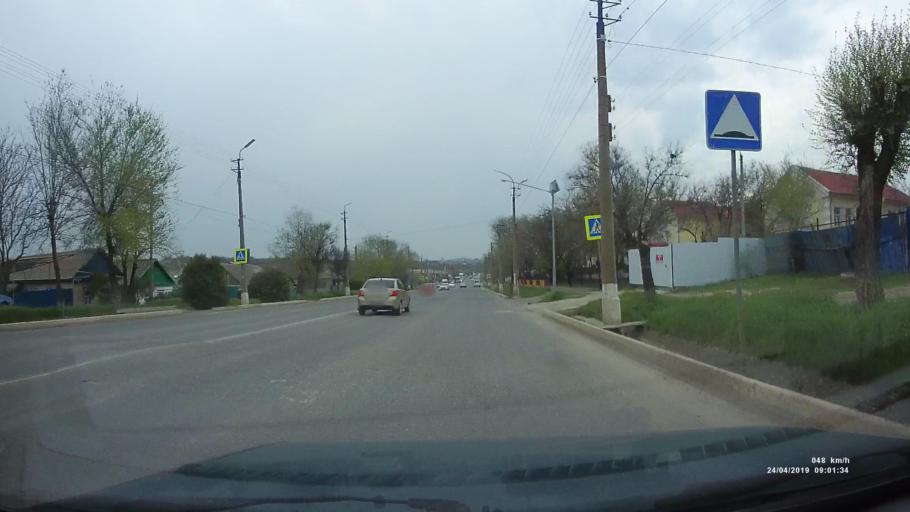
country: RU
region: Kalmykiya
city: Elista
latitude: 46.3127
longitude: 44.2264
